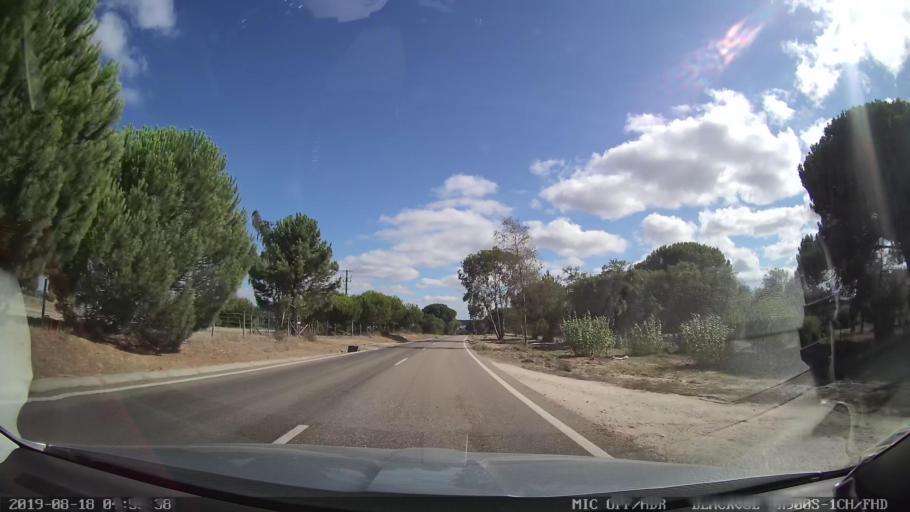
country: PT
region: Santarem
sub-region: Benavente
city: Poceirao
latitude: 38.8728
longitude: -8.7469
